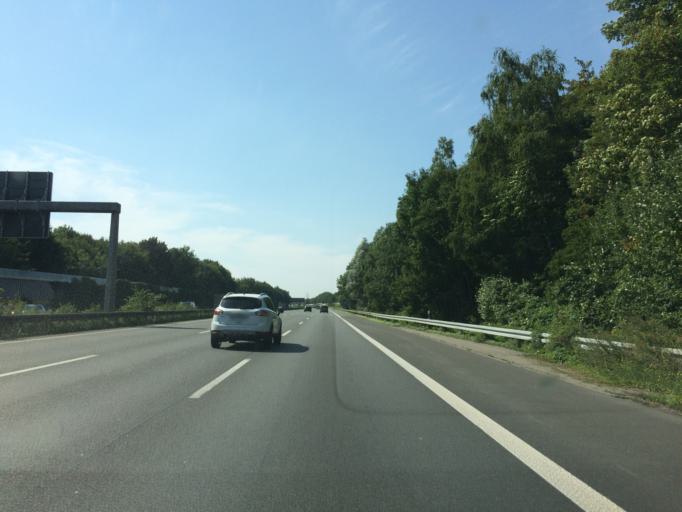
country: DE
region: North Rhine-Westphalia
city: Kamen
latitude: 51.6011
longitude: 7.6735
